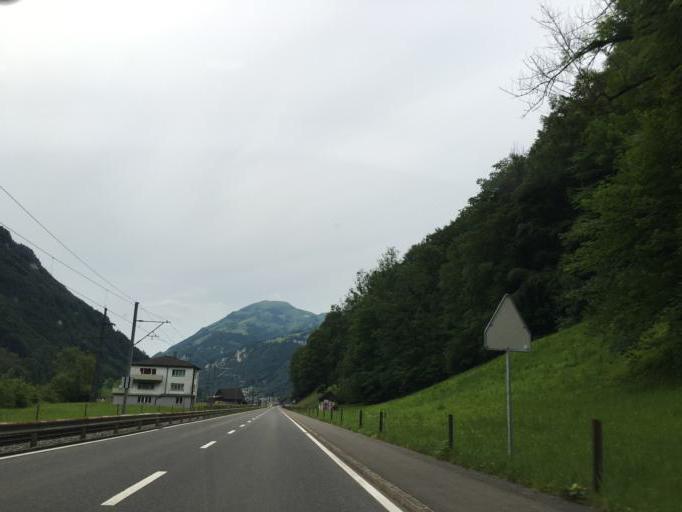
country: CH
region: Nidwalden
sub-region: Nidwalden
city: Wolfenschiessen
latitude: 46.8833
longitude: 8.3794
